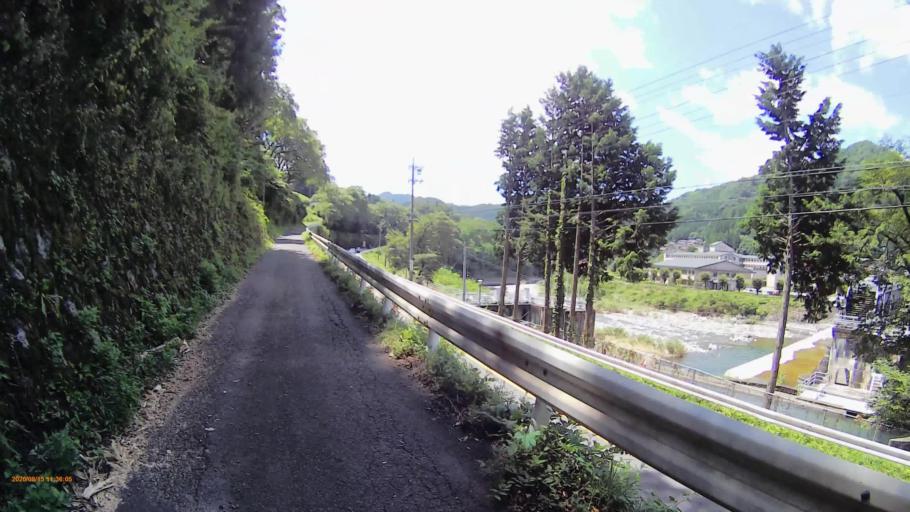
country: JP
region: Nagano
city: Ina
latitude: 35.8361
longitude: 137.6871
